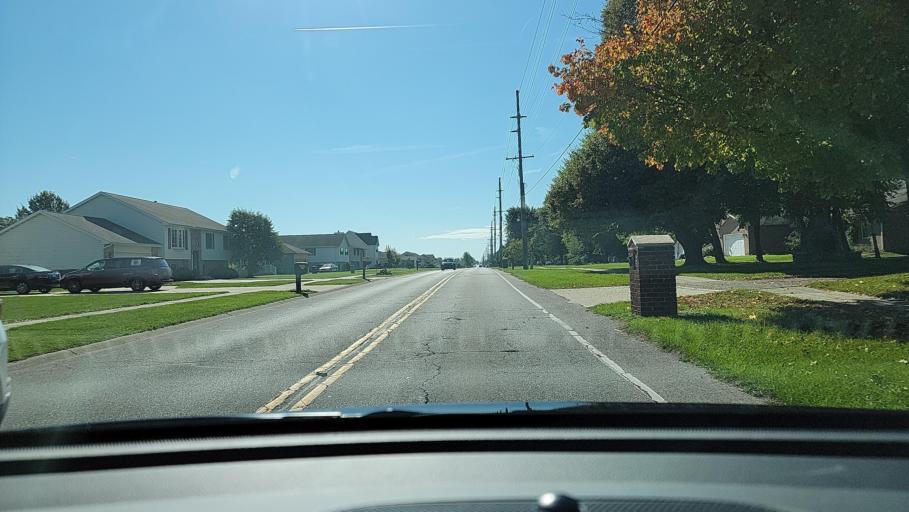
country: US
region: Indiana
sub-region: Porter County
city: Portage
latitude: 41.5674
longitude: -87.1635
